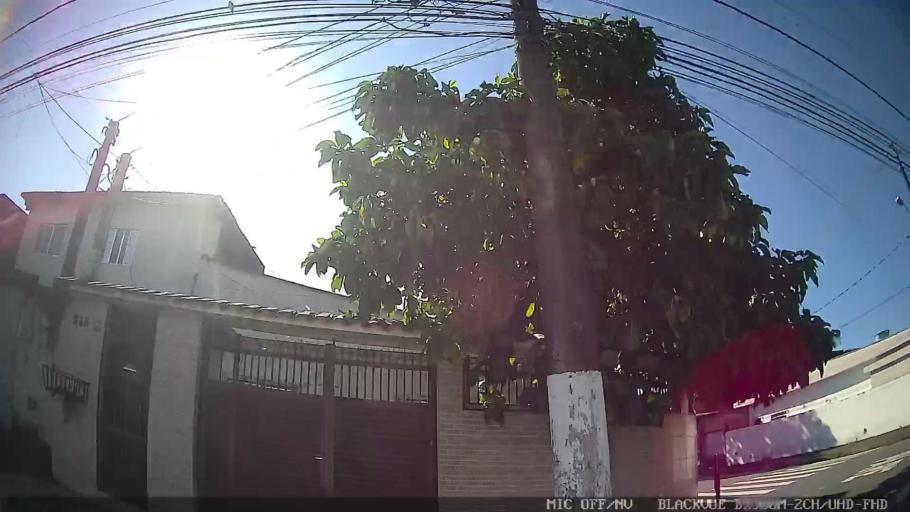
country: BR
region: Sao Paulo
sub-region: Santos
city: Santos
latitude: -23.9513
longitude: -46.2853
